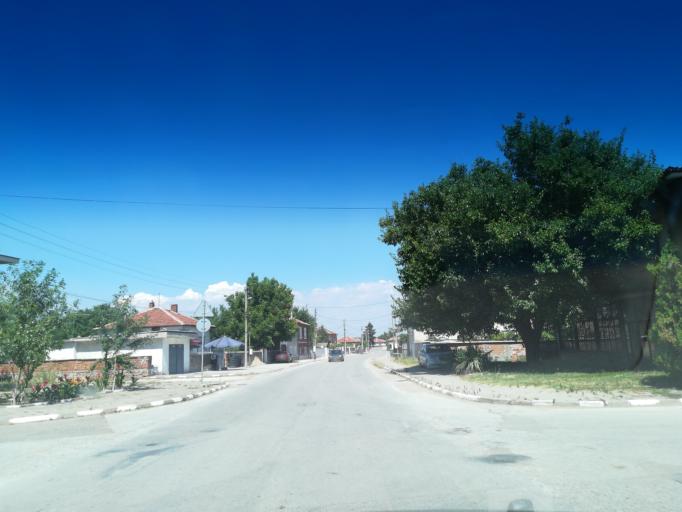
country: BG
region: Plovdiv
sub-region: Obshtina Sadovo
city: Sadovo
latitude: 42.0257
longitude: 25.1062
